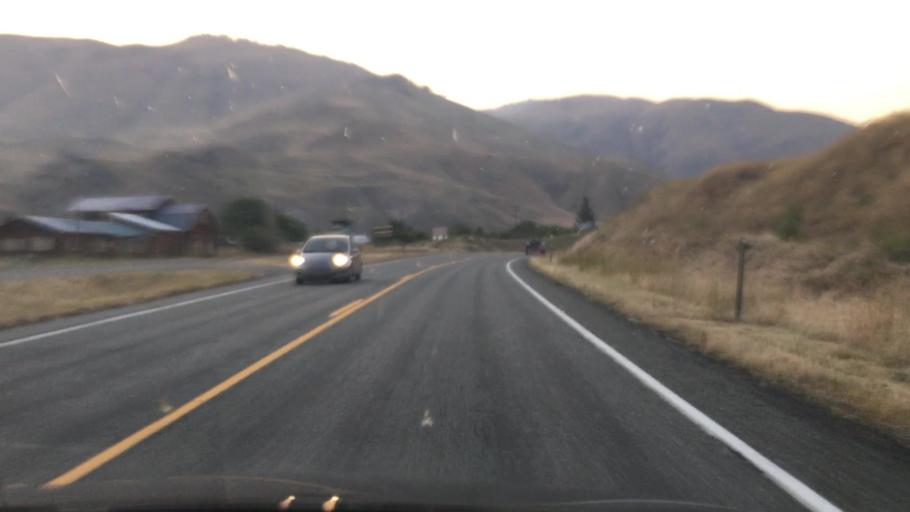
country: US
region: Idaho
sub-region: Idaho County
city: Grangeville
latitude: 45.5340
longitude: -116.3069
